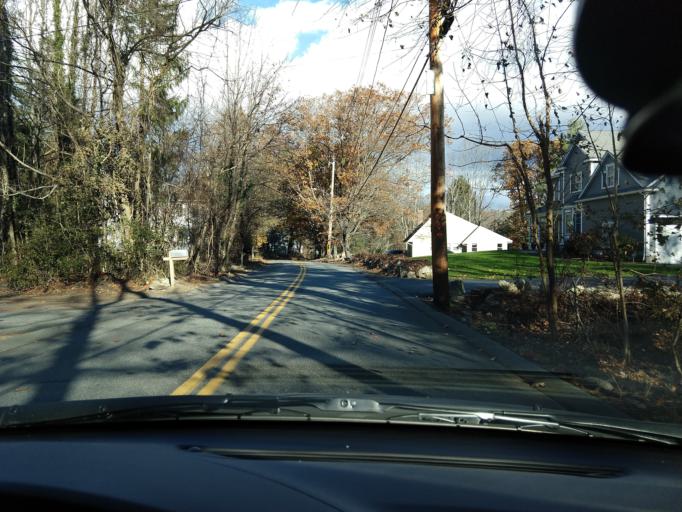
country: US
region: Massachusetts
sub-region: Middlesex County
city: Bedford
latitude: 42.4997
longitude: -71.2471
